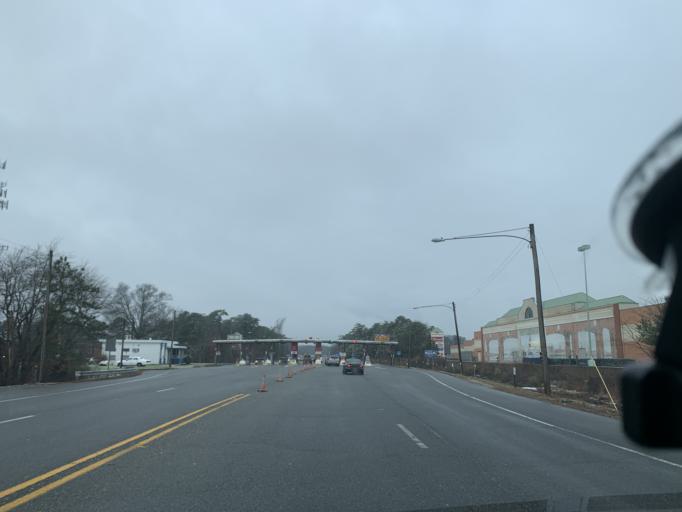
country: US
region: New Jersey
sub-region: Atlantic County
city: Pomona
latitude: 39.4498
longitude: -74.6297
